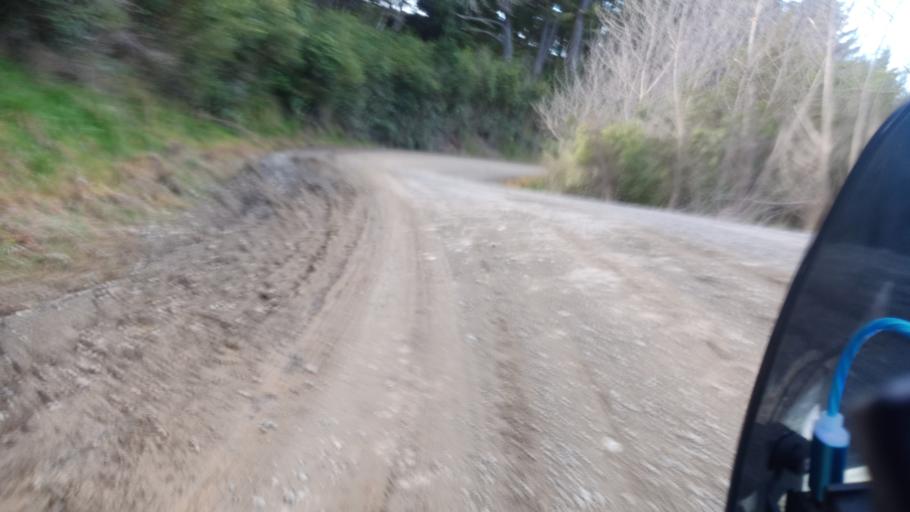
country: NZ
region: Gisborne
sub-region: Gisborne District
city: Gisborne
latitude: -38.1398
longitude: 178.1967
